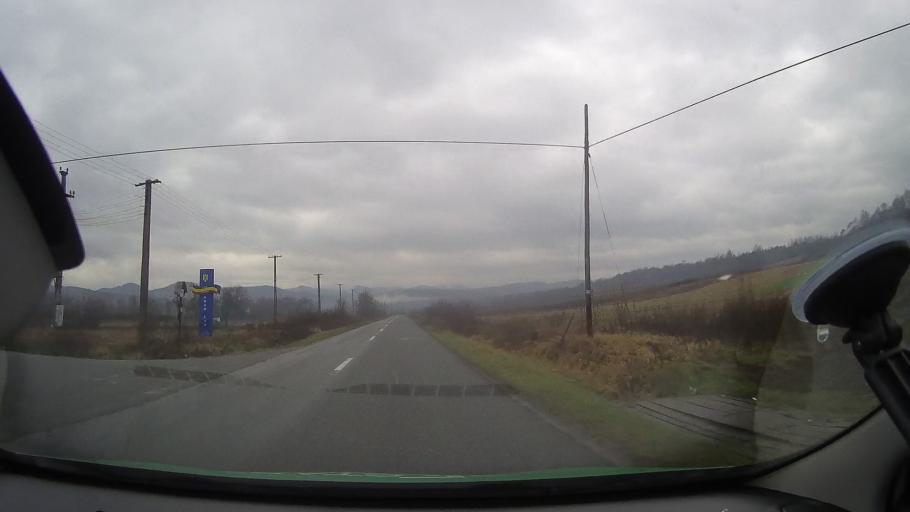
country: RO
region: Arad
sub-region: Comuna Gurahont
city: Gurahont
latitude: 46.2540
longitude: 22.3341
